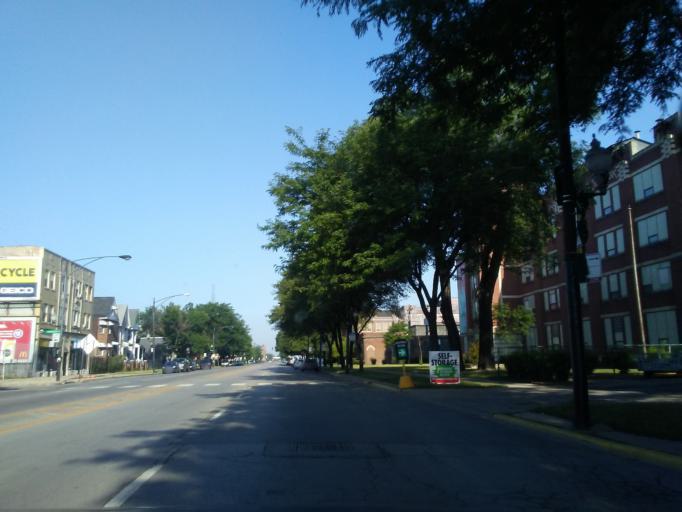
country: US
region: Illinois
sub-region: Cook County
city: Oak Park
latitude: 41.9245
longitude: -87.7288
